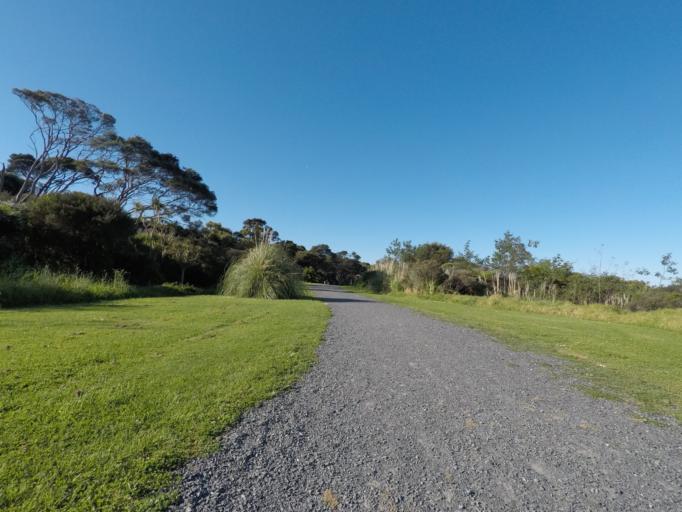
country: NZ
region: Auckland
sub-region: Auckland
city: Rosebank
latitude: -36.8465
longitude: 174.6551
